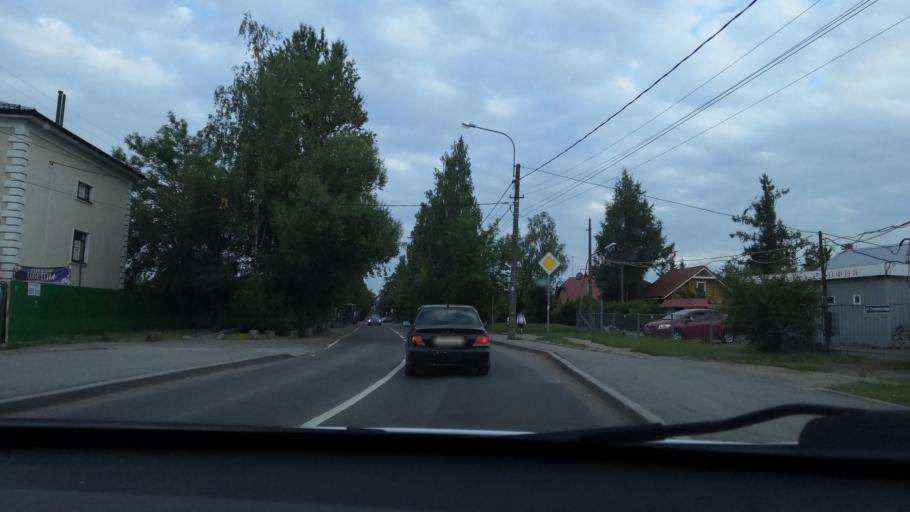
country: RU
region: St.-Petersburg
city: Pushkin
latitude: 59.7026
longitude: 30.4075
